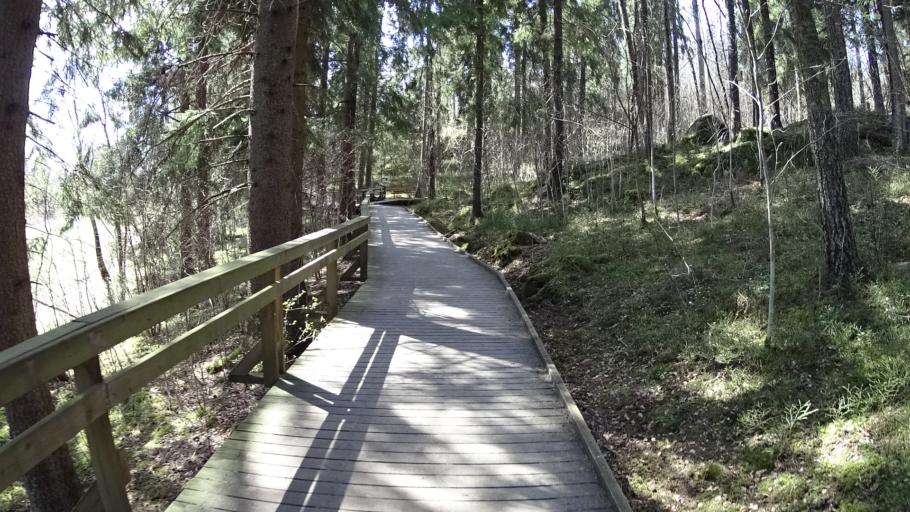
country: FI
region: Uusimaa
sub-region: Helsinki
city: Siuntio
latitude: 60.1688
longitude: 24.2151
